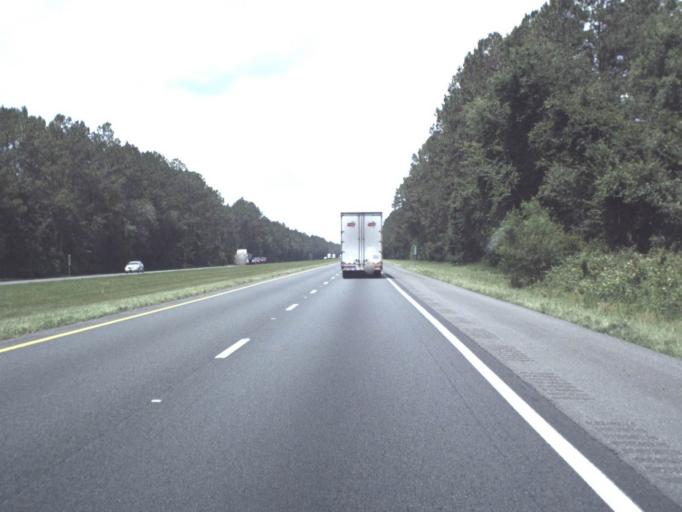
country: US
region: Florida
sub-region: Baker County
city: Macclenny
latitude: 30.2528
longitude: -82.2067
